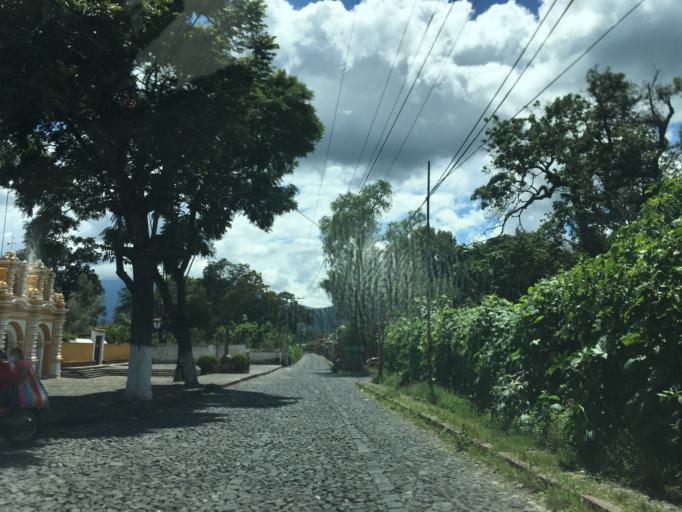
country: GT
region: Sacatepequez
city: Antigua Guatemala
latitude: 14.5457
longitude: -90.7293
